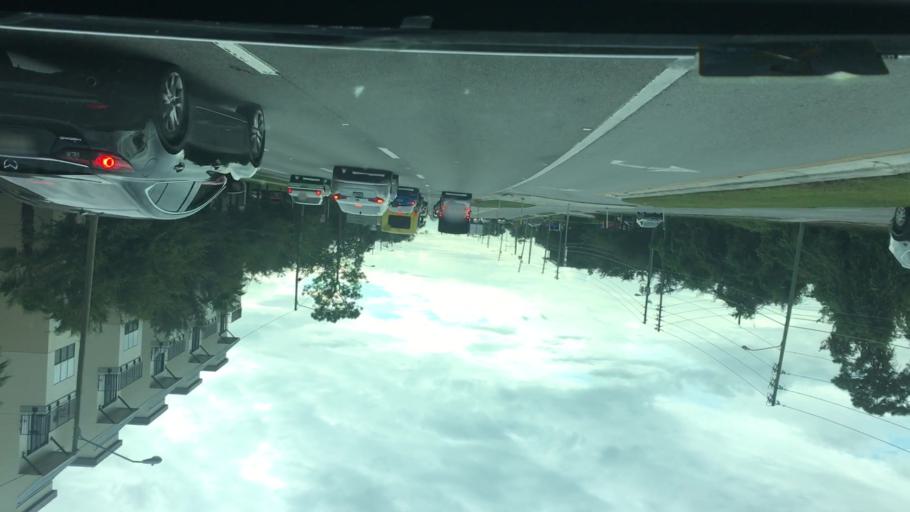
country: US
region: Florida
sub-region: Orange County
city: Alafaya
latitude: 28.5858
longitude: -81.2079
